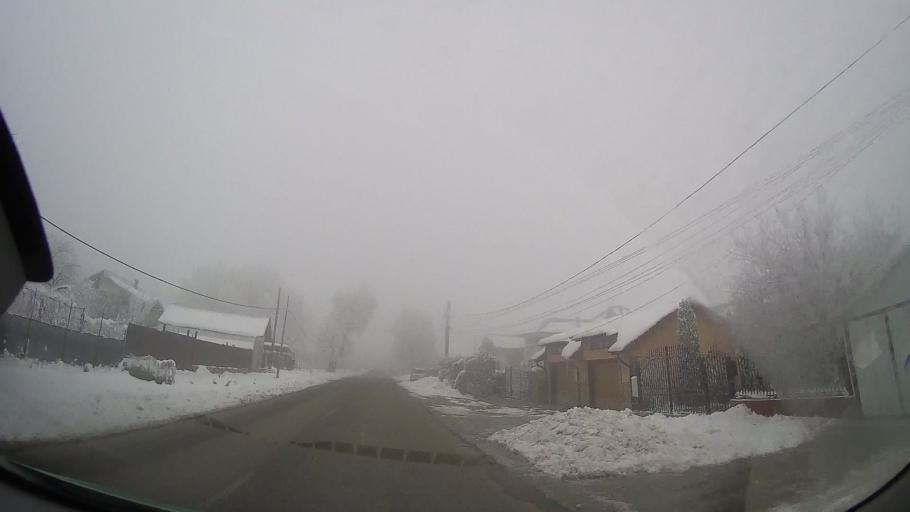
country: RO
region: Neamt
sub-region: Comuna Sabaoani
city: Sabaoani
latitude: 47.0221
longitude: 26.8639
